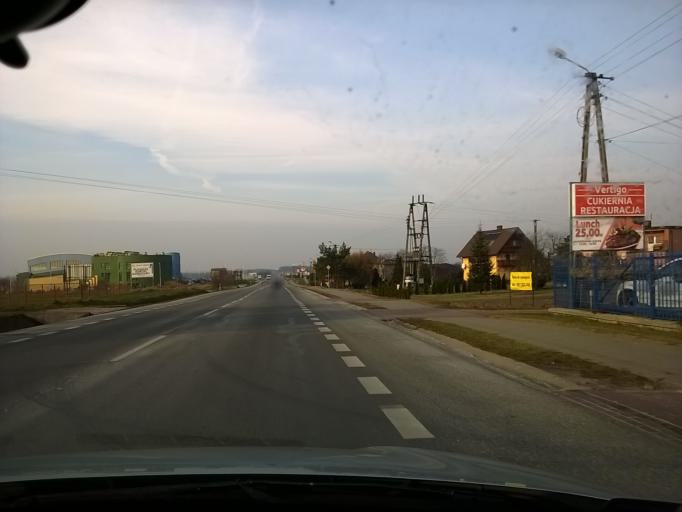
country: PL
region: Silesian Voivodeship
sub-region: Powiat gliwicki
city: Paniowki
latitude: 50.2346
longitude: 18.7847
